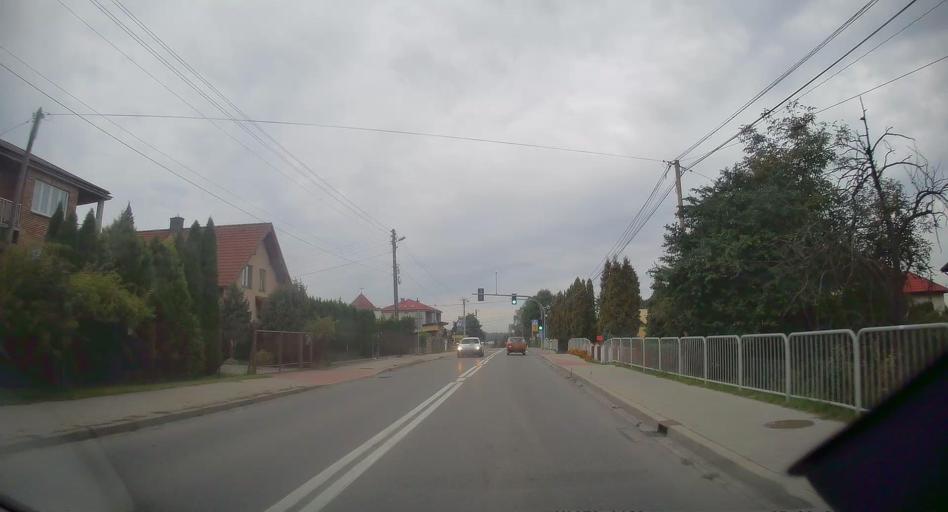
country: PL
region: Lesser Poland Voivodeship
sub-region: Powiat wielicki
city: Podleze
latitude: 50.0135
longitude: 20.1634
